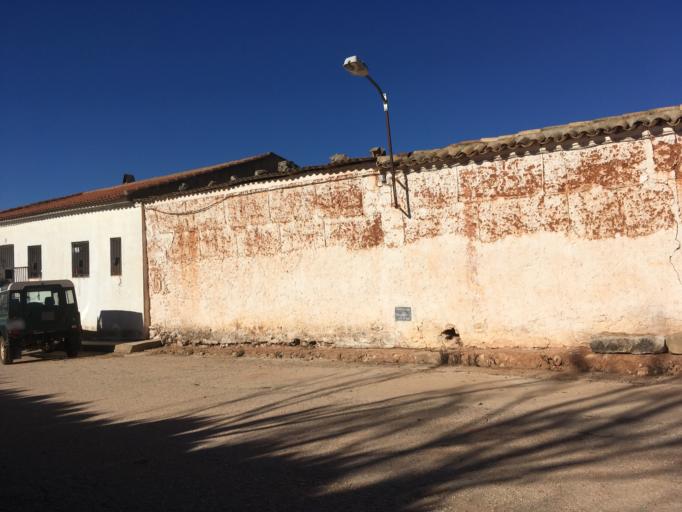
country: ES
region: Castille-La Mancha
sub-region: Provincia de Cuenca
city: Atalaya del Canavate
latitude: 39.5494
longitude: -2.2473
